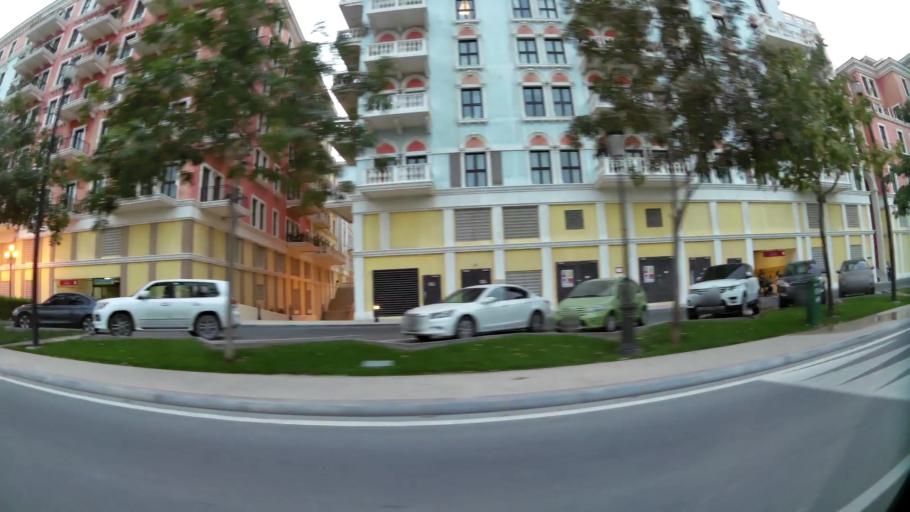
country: QA
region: Baladiyat ad Dawhah
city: Doha
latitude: 25.3761
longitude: 51.5460
